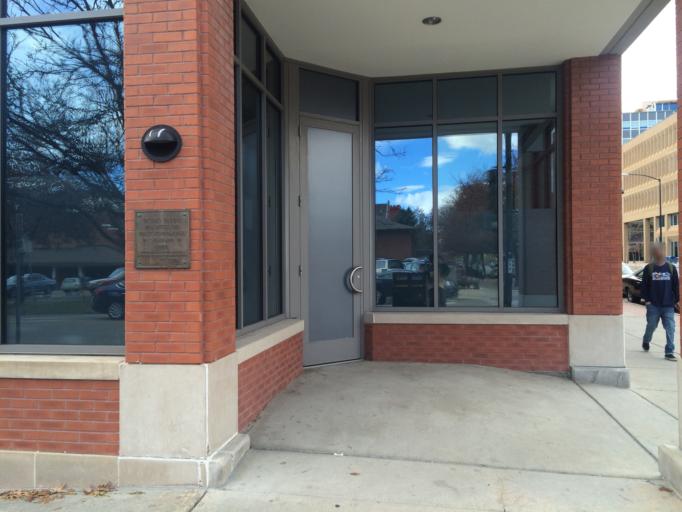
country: US
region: Colorado
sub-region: Boulder County
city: Boulder
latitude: 40.0176
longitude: -105.2757
